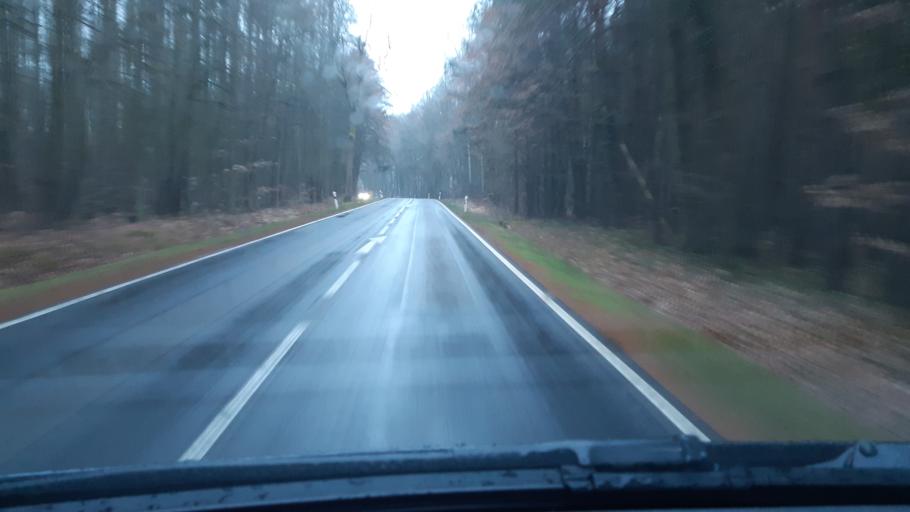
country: DE
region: Brandenburg
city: Milmersdorf
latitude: 53.1581
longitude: 13.6027
